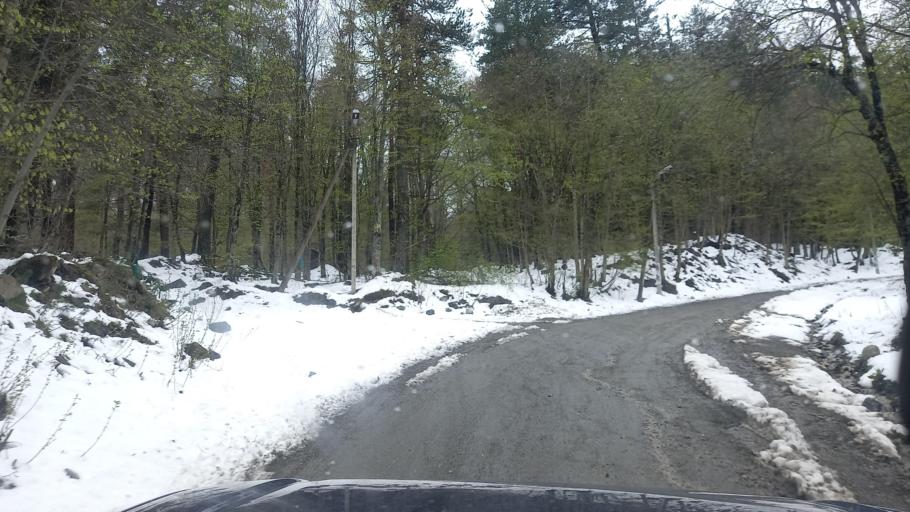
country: RU
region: North Ossetia
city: Mizur
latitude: 42.7896
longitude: 43.9088
